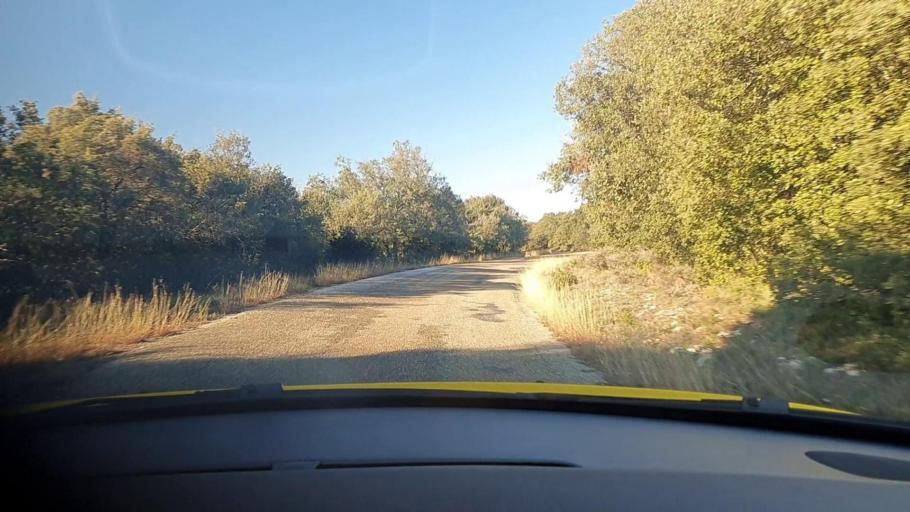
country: FR
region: Languedoc-Roussillon
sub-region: Departement du Gard
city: Goudargues
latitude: 44.1695
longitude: 4.3518
